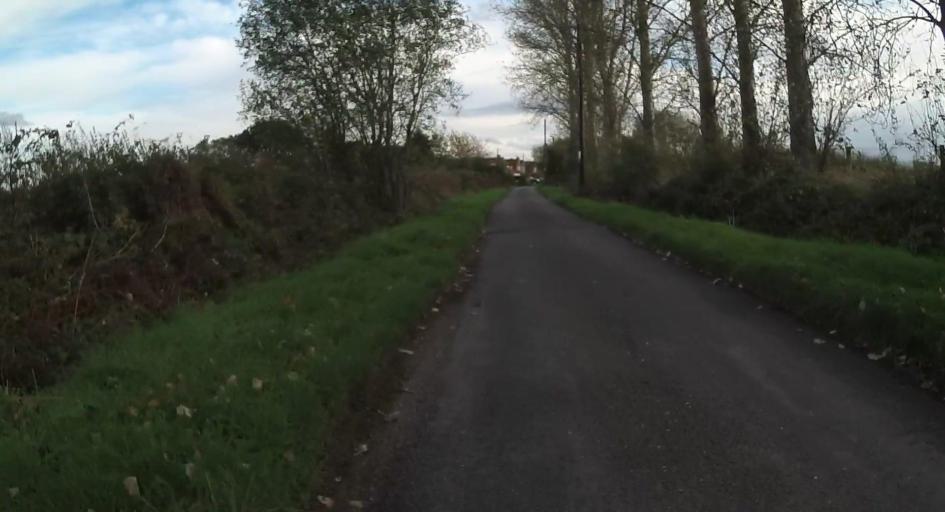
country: GB
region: England
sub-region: Wokingham
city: Swallowfield
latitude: 51.3683
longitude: -0.9551
